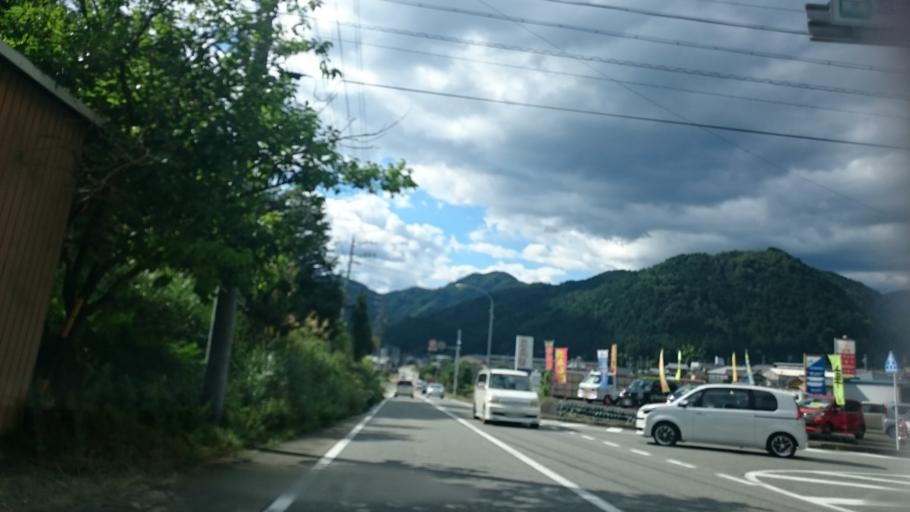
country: JP
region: Gifu
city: Gujo
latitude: 35.7641
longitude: 137.2900
